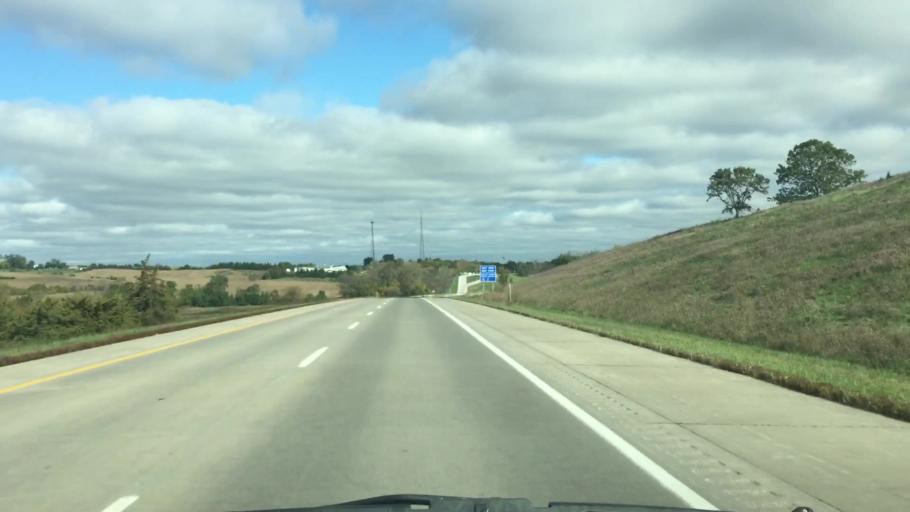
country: US
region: Iowa
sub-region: Clarke County
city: Osceola
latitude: 41.0040
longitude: -93.7978
